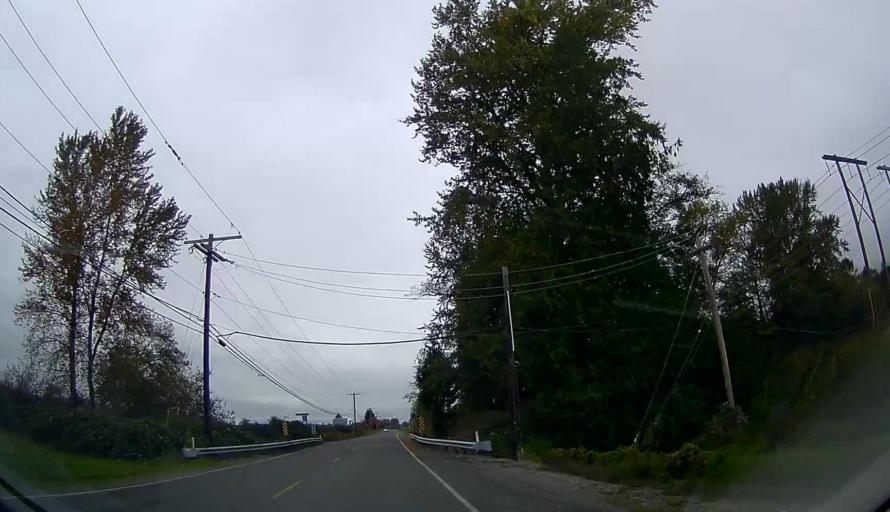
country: US
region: Washington
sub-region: Skagit County
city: Sedro-Woolley
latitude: 48.5256
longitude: -122.1306
